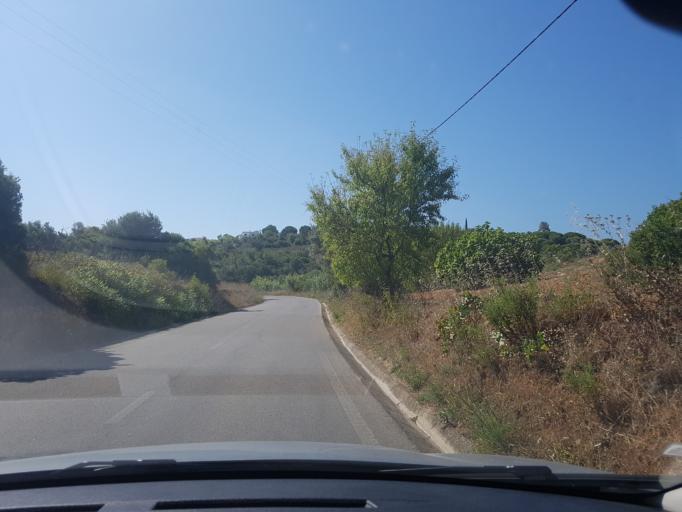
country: PT
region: Faro
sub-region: Lagoa
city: Carvoeiro
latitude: 37.1024
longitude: -8.4283
